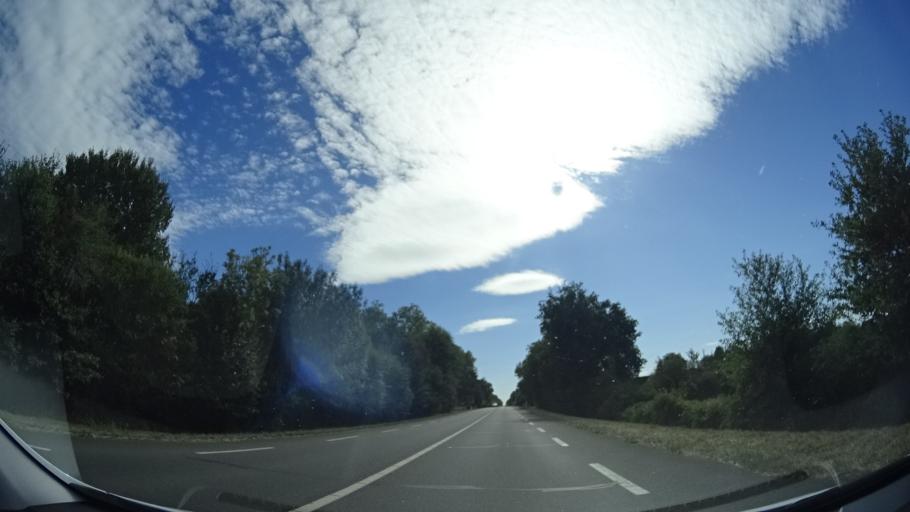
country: FR
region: Centre
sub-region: Departement du Loiret
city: Vitry-aux-Loges
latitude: 47.9385
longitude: 2.3530
